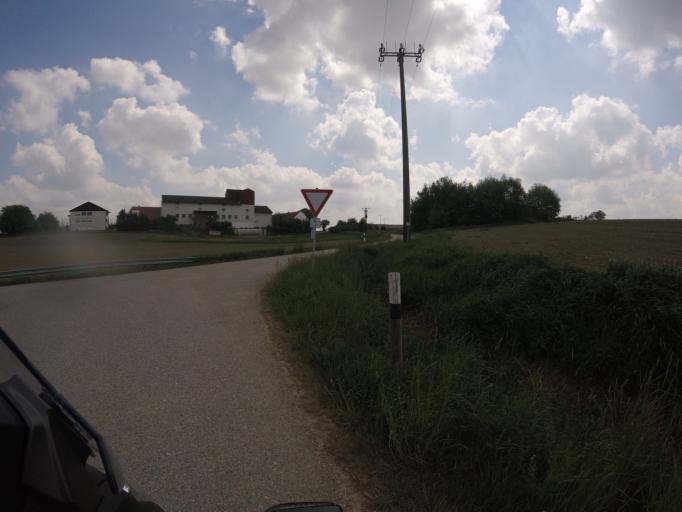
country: DE
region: Bavaria
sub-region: Upper Bavaria
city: Au in der Hallertau
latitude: 48.6050
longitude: 11.7059
